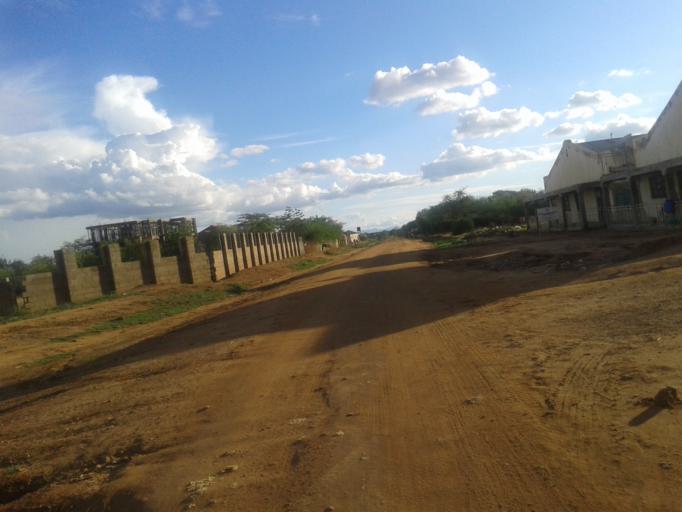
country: UG
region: Northern Region
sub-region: Kotido District
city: Kotido
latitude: 3.0035
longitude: 34.1120
